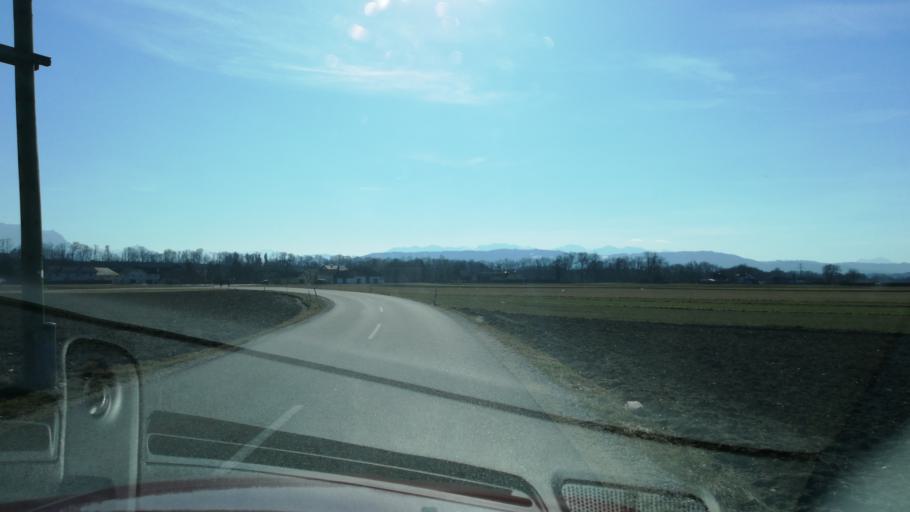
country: AT
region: Upper Austria
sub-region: Politischer Bezirk Vocklabruck
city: Redlham
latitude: 48.0181
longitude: 13.7419
